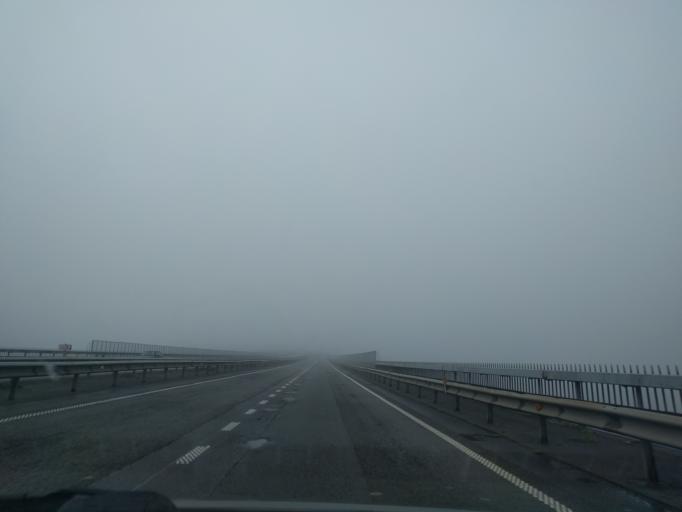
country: BE
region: Wallonia
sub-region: Province de Namur
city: Dinant
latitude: 50.2406
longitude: 4.9215
